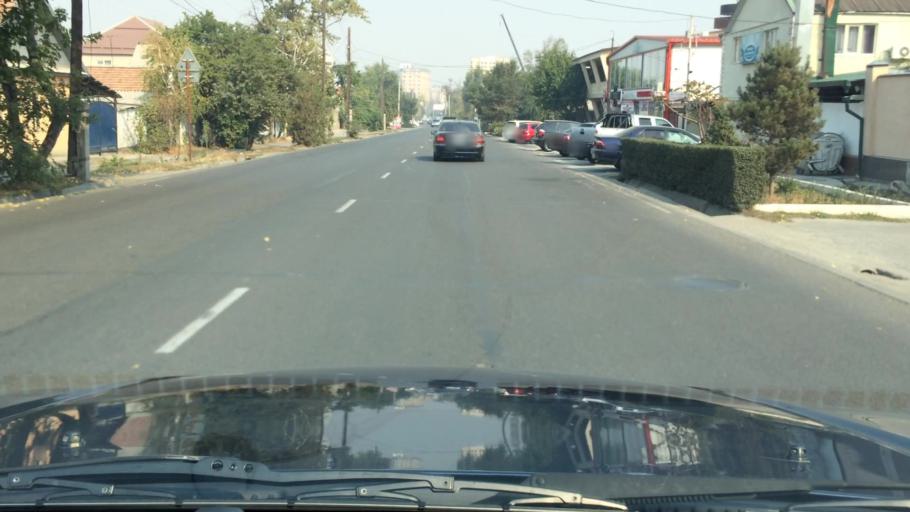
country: KG
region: Chuy
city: Bishkek
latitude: 42.8581
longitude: 74.5999
